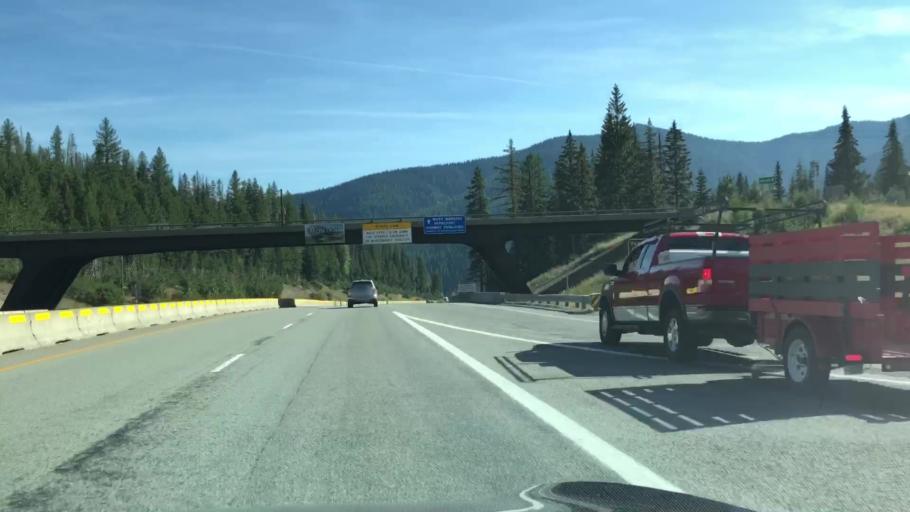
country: US
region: Idaho
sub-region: Shoshone County
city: Wallace
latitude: 47.4541
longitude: -115.6947
